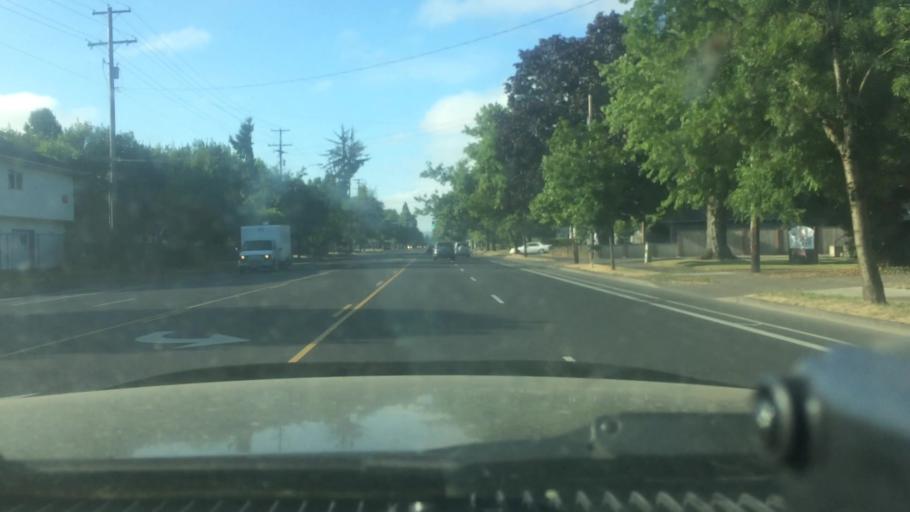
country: US
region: Oregon
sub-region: Lane County
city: Eugene
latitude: 44.0897
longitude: -123.1257
